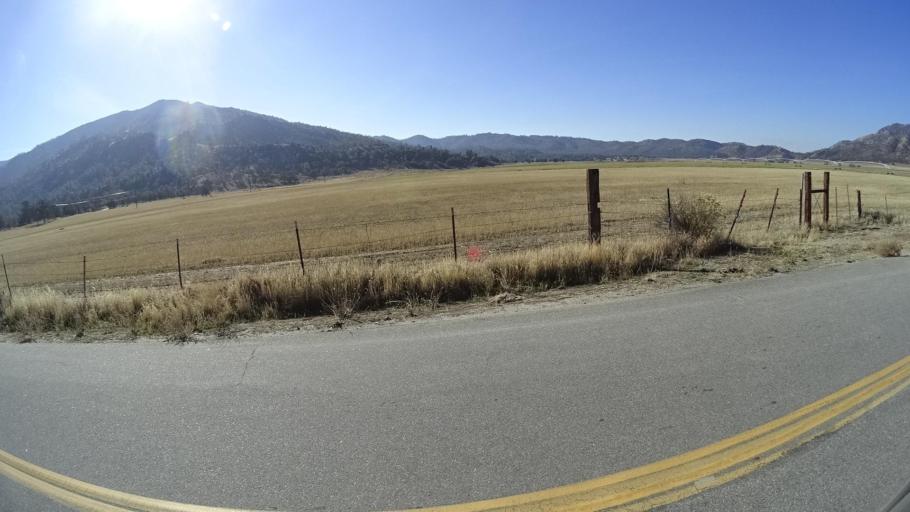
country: US
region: California
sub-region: Kern County
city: Bodfish
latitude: 35.4013
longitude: -118.5223
